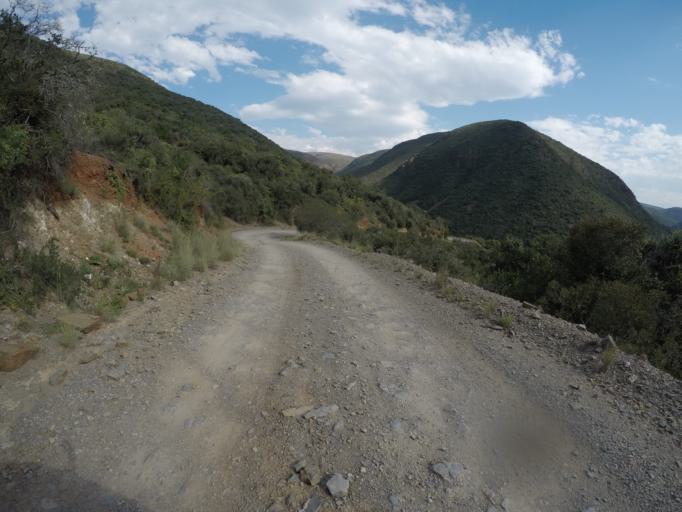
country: ZA
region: Eastern Cape
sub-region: Cacadu District Municipality
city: Kareedouw
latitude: -33.6480
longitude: 24.3385
